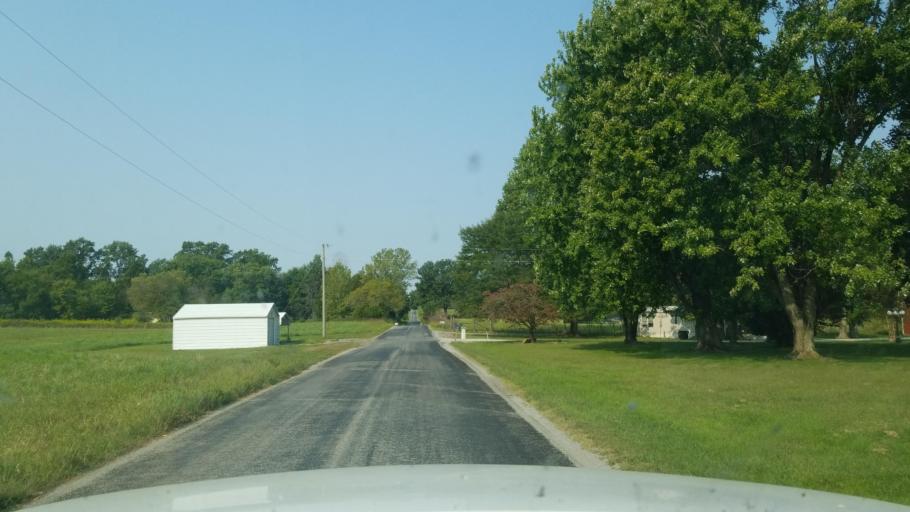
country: US
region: Illinois
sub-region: Saline County
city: Carrier Mills
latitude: 37.7906
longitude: -88.6625
